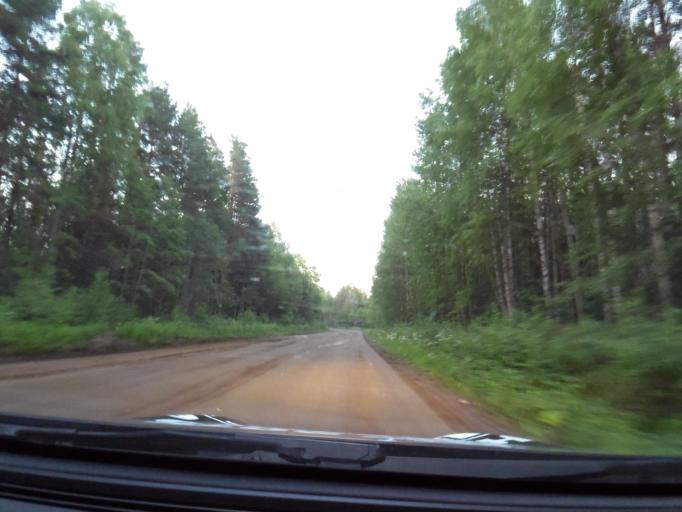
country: RU
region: Leningrad
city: Voznesen'ye
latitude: 60.8558
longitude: 35.9219
